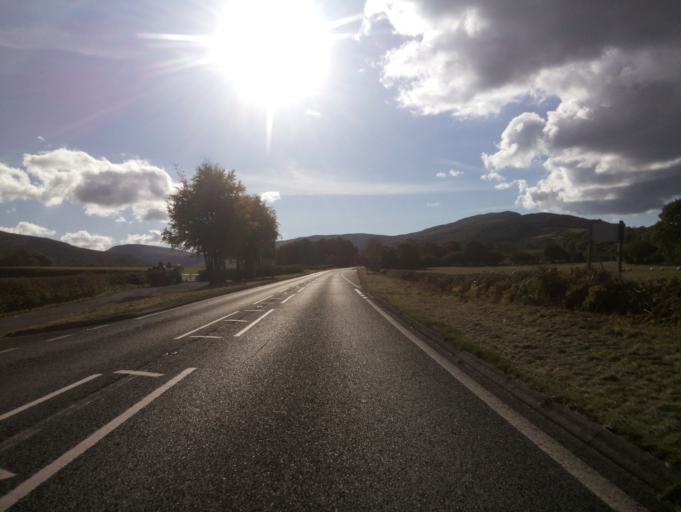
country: GB
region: Wales
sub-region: Sir Powys
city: Brecon
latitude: 51.9142
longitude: -3.4704
